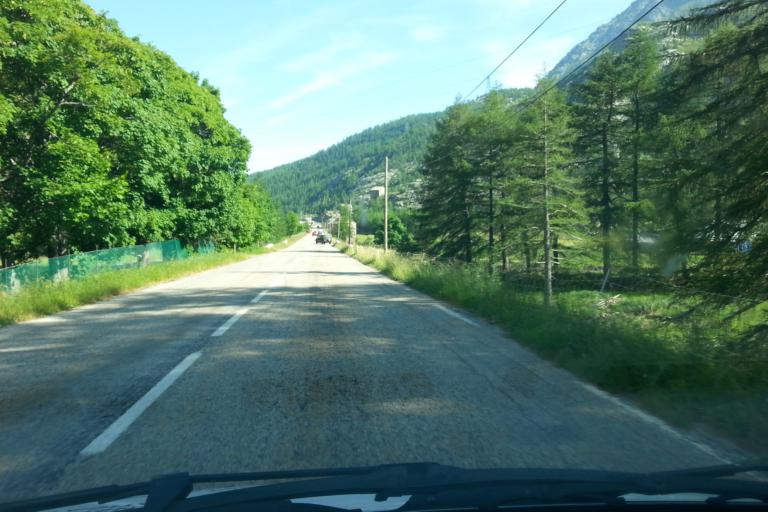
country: IT
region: Piedmont
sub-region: Provincia di Torino
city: Moncenisio
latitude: 45.2138
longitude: 6.9563
